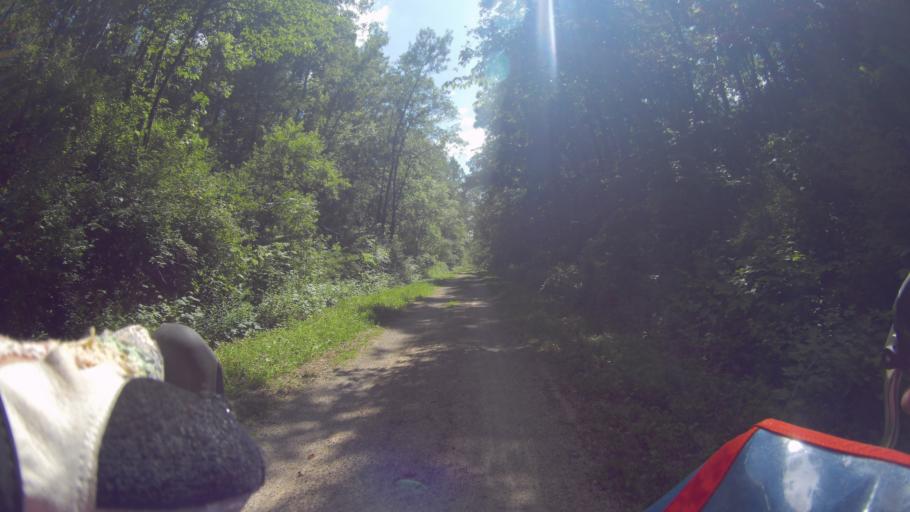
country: US
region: Wisconsin
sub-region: Dane County
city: Fitchburg
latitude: 42.9396
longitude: -89.4879
